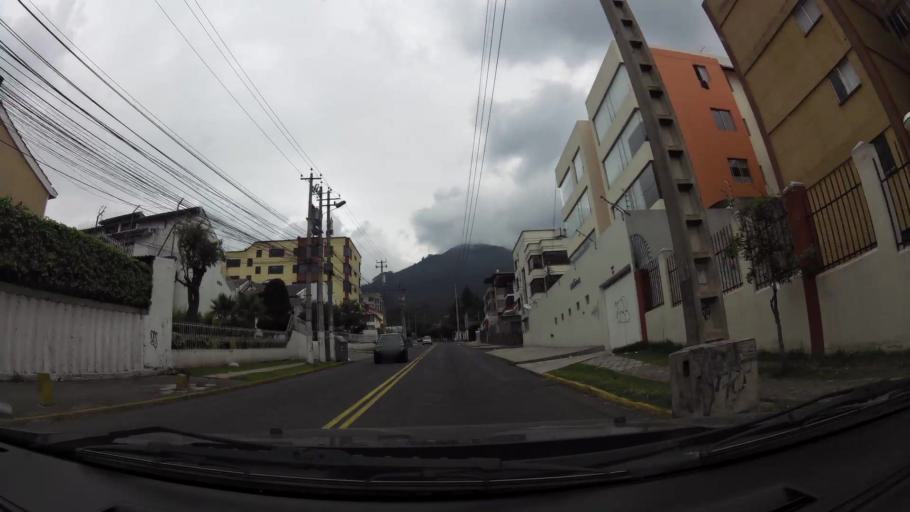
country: EC
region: Pichincha
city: Quito
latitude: -0.1755
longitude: -78.4991
